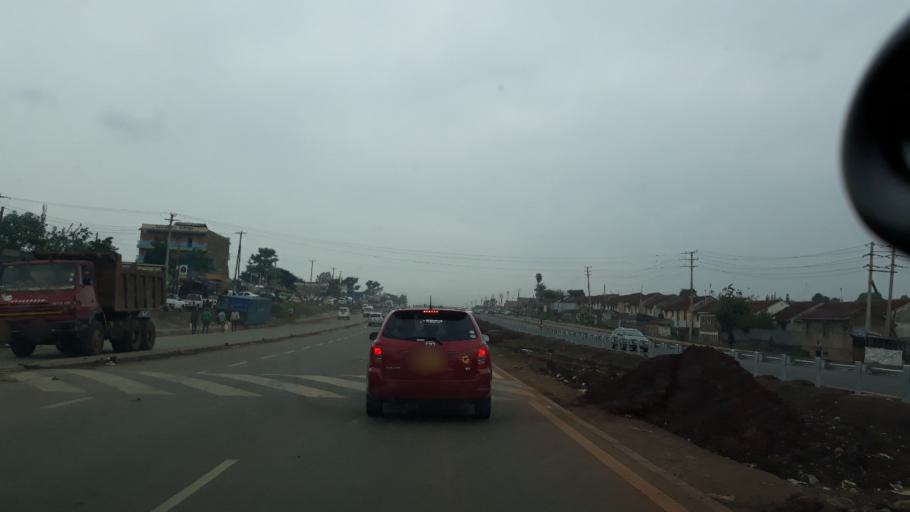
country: KE
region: Nairobi Area
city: Pumwani
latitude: -1.2651
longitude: 36.8796
